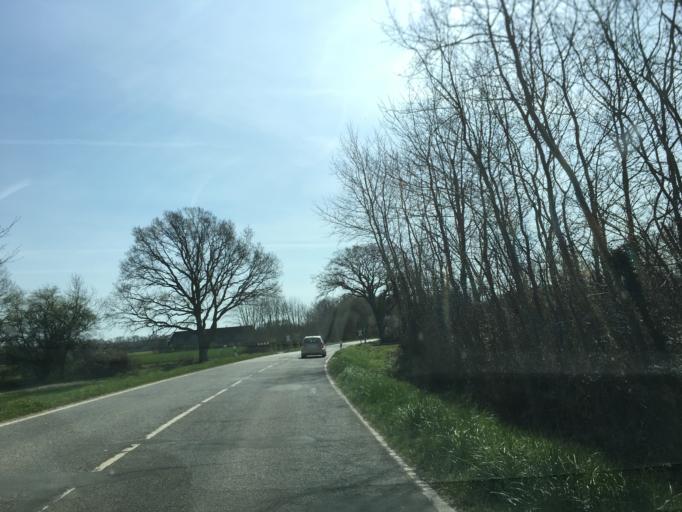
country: DE
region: Schleswig-Holstein
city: Ottendorf
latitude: 54.3817
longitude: 10.0581
